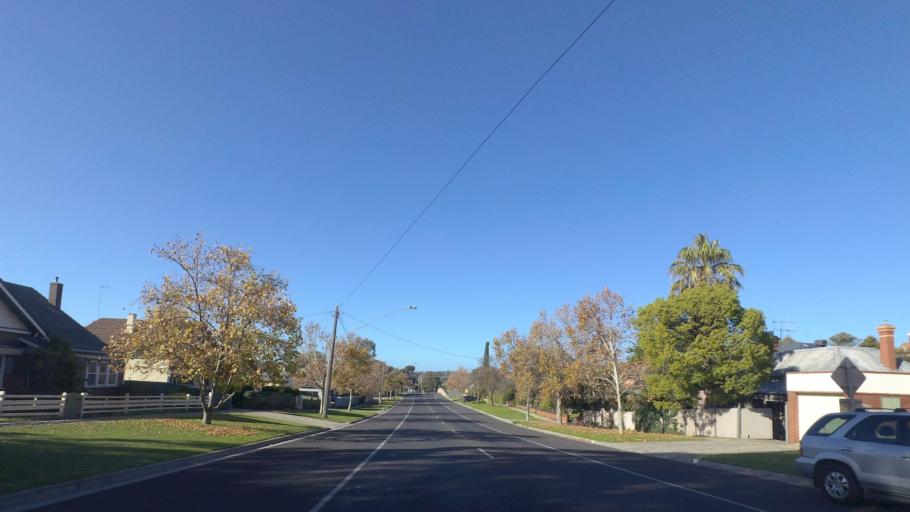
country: AU
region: Victoria
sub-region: Greater Bendigo
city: Quarry Hill
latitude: -36.7693
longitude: 144.2831
